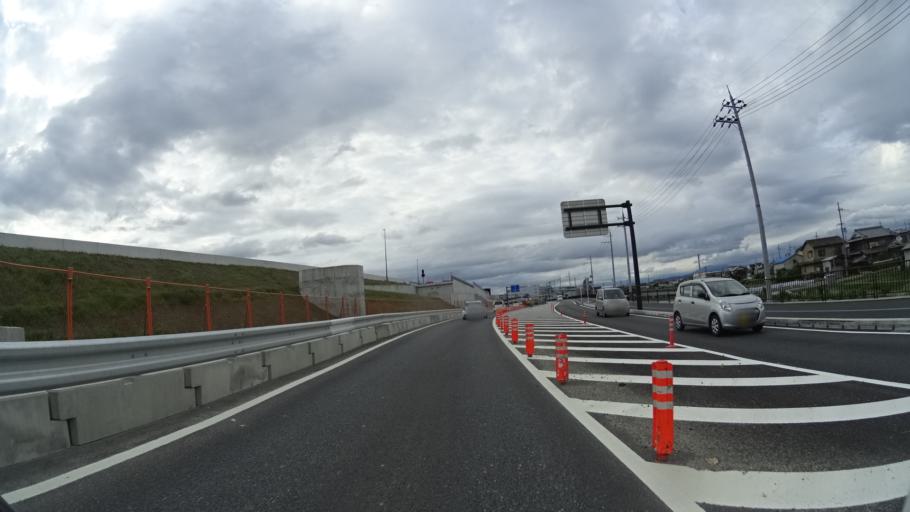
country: JP
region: Kyoto
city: Tanabe
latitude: 34.8482
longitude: 135.7627
